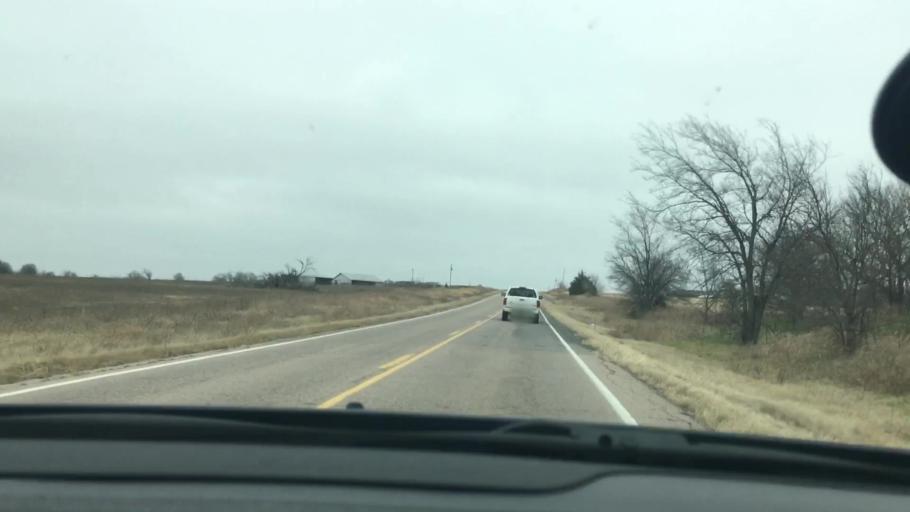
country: US
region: Oklahoma
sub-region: Marshall County
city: Madill
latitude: 34.1163
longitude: -96.7356
